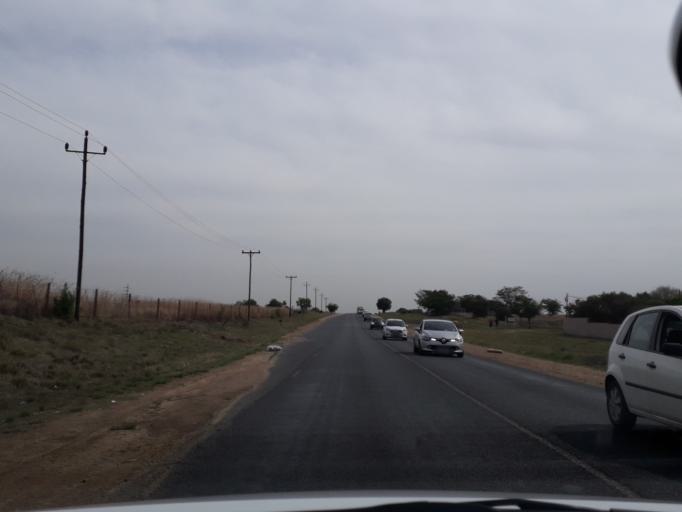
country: ZA
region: Gauteng
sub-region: City of Johannesburg Metropolitan Municipality
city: Diepsloot
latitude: -25.9930
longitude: 28.0492
